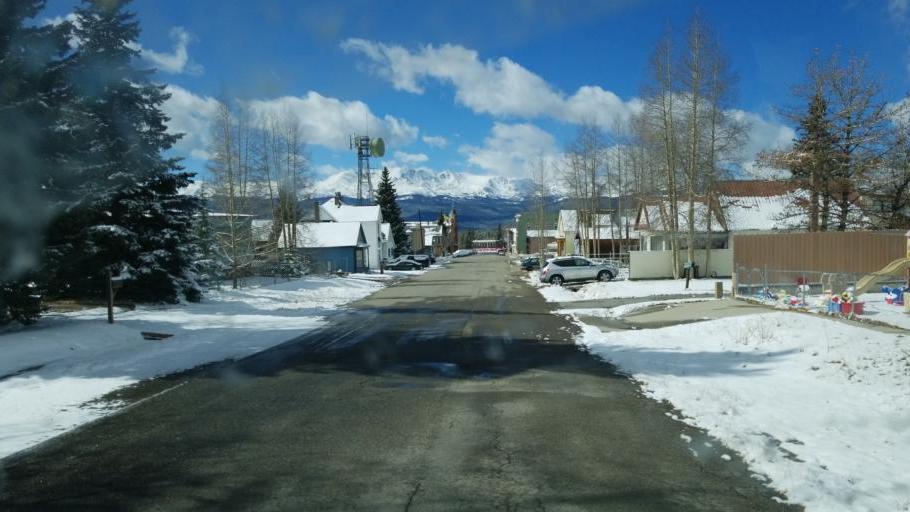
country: US
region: Colorado
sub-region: Lake County
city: Leadville
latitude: 39.2488
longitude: -106.2881
